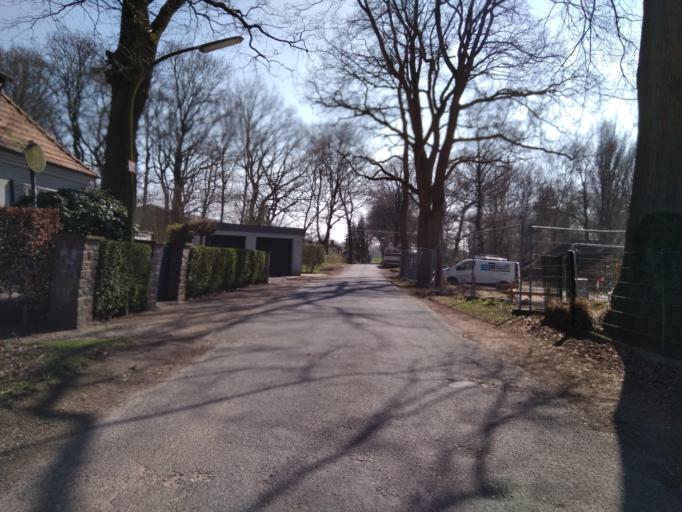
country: DE
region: North Rhine-Westphalia
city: Dorsten
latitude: 51.6471
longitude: 6.9669
